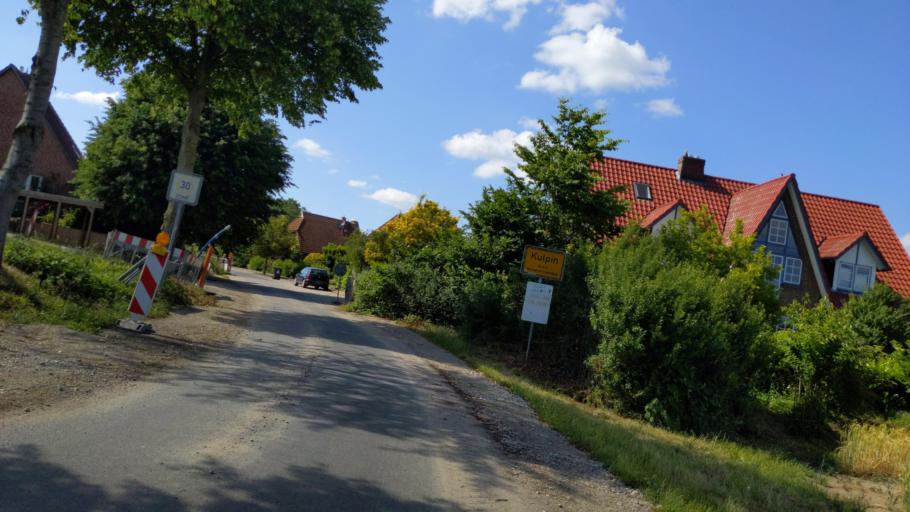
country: DE
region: Schleswig-Holstein
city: Kulpin
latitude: 53.7071
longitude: 10.7007
